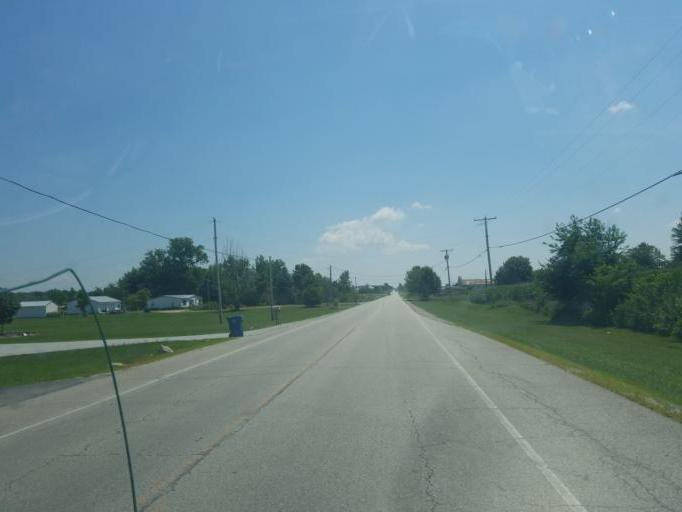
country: US
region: Ohio
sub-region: Shelby County
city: Botkins
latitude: 40.4384
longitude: -84.1785
